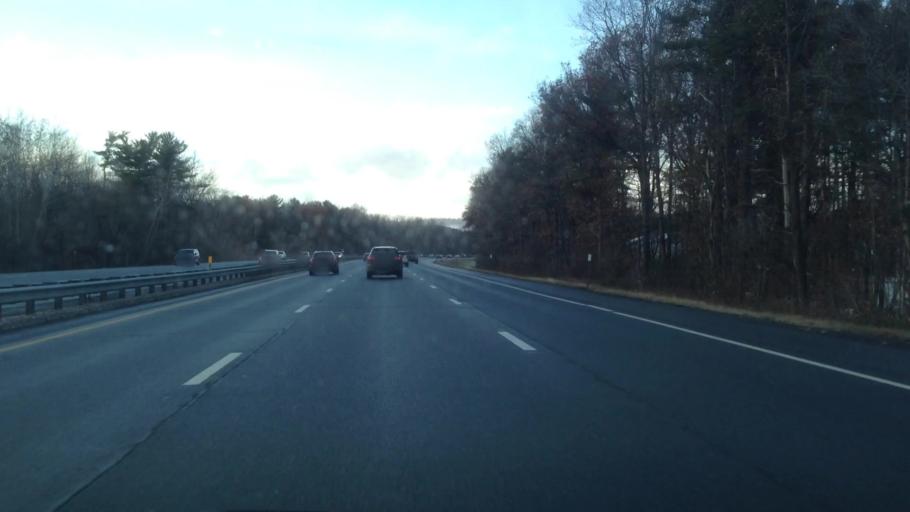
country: US
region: New York
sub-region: Schenectady County
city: Rotterdam
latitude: 42.7817
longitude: -74.0066
